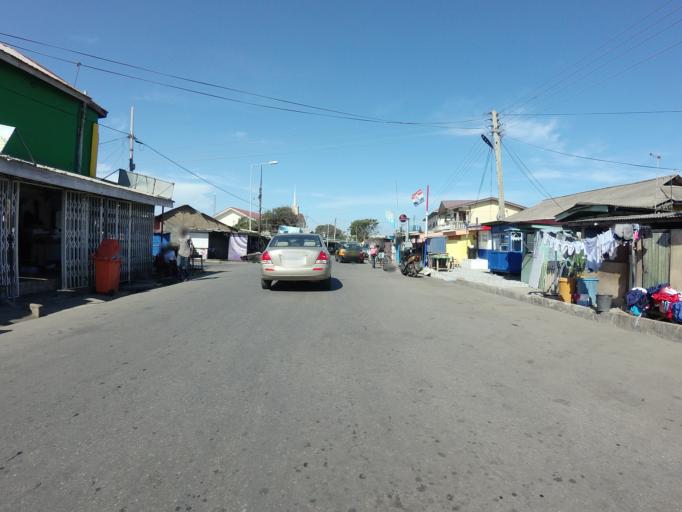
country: GH
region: Greater Accra
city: Accra
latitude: 5.5611
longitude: -0.1541
